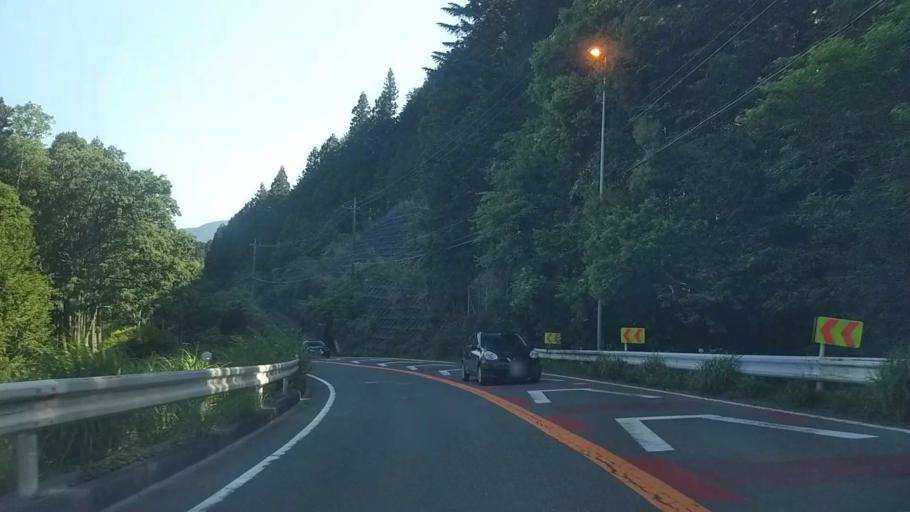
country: JP
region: Shizuoka
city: Fujinomiya
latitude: 35.2115
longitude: 138.5194
